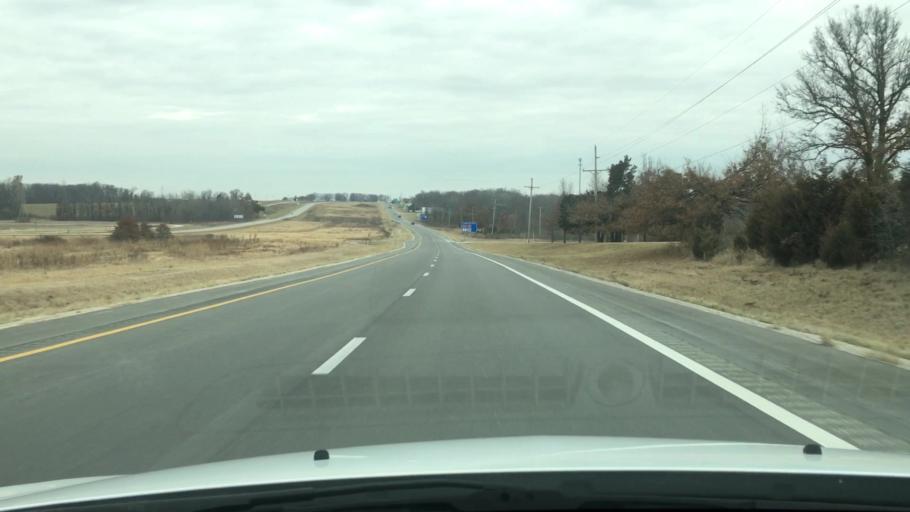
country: US
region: Missouri
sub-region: Audrain County
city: Mexico
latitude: 39.1013
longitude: -91.8966
